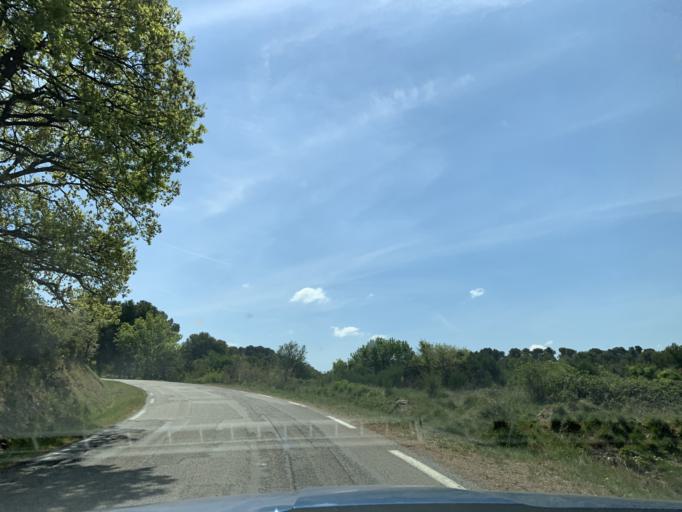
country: FR
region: Provence-Alpes-Cote d'Azur
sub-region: Departement du Vaucluse
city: Saint-Didier
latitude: 43.9944
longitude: 5.1058
